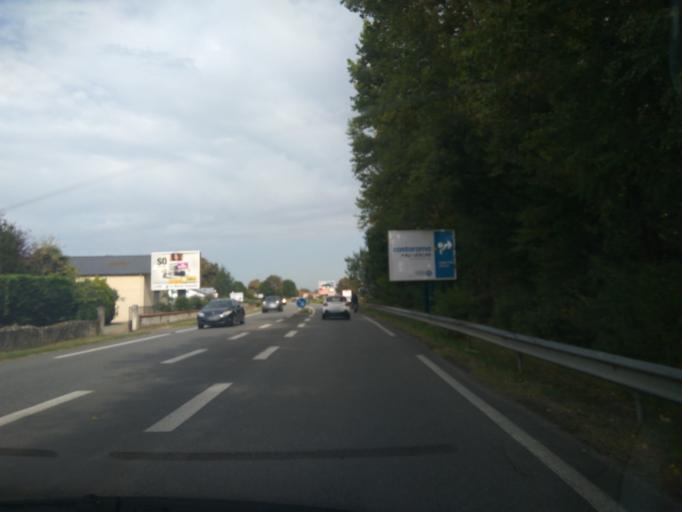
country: FR
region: Aquitaine
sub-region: Departement des Pyrenees-Atlantiques
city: Artiguelouve
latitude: 43.3119
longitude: -0.4504
